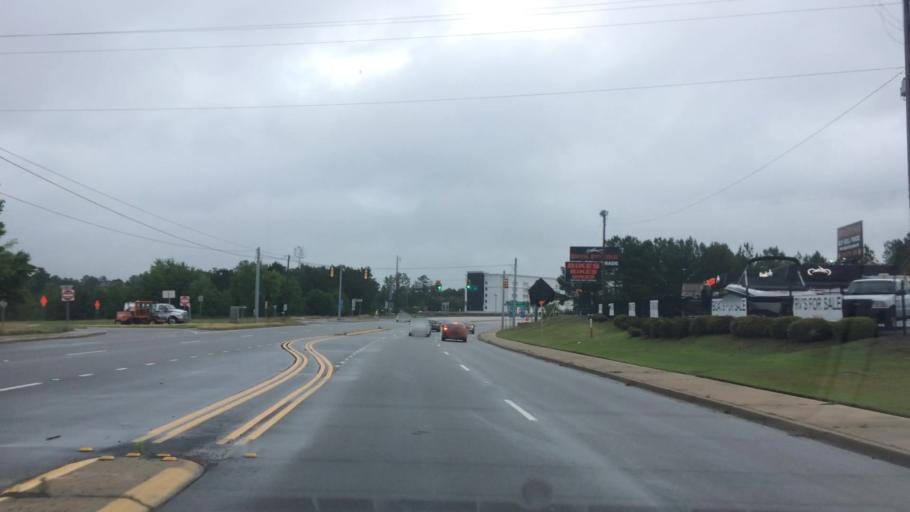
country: US
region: South Carolina
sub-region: Richland County
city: Dentsville
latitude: 34.0805
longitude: -80.9419
